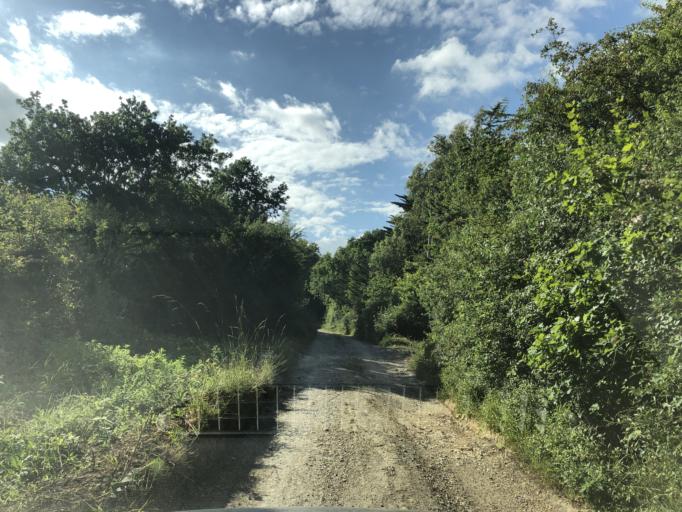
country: GB
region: England
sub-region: Isle of Wight
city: Shalfleet
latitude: 50.7119
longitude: -1.4438
